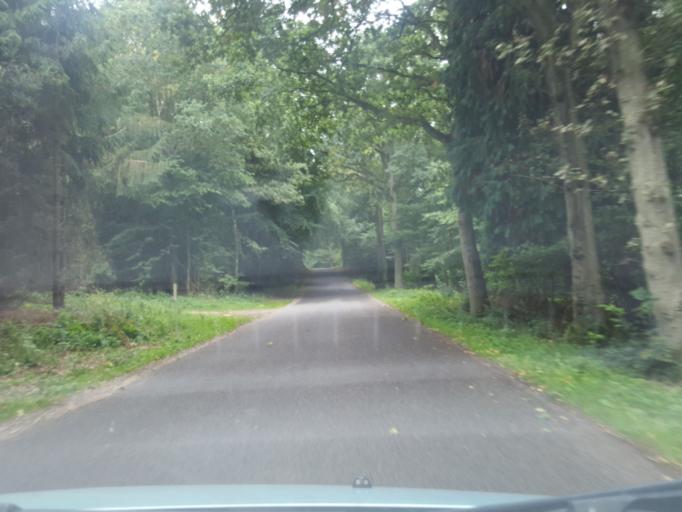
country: DK
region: Zealand
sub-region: Soro Kommune
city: Dianalund
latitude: 55.4788
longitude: 11.5193
